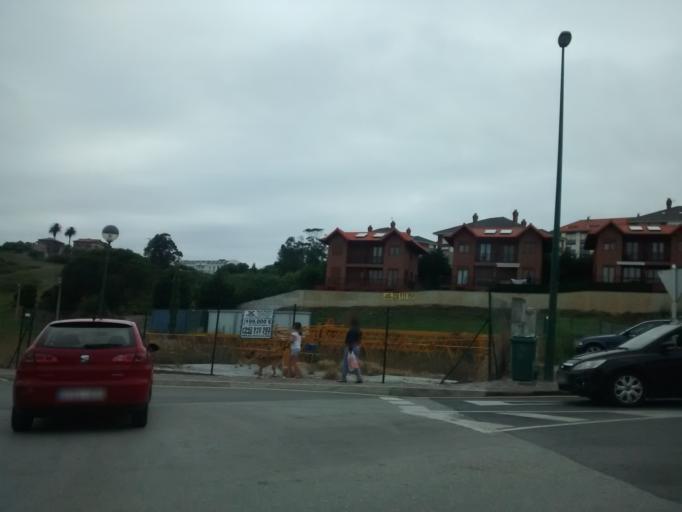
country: ES
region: Cantabria
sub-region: Provincia de Cantabria
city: Suances
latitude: 43.4313
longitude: -4.0370
